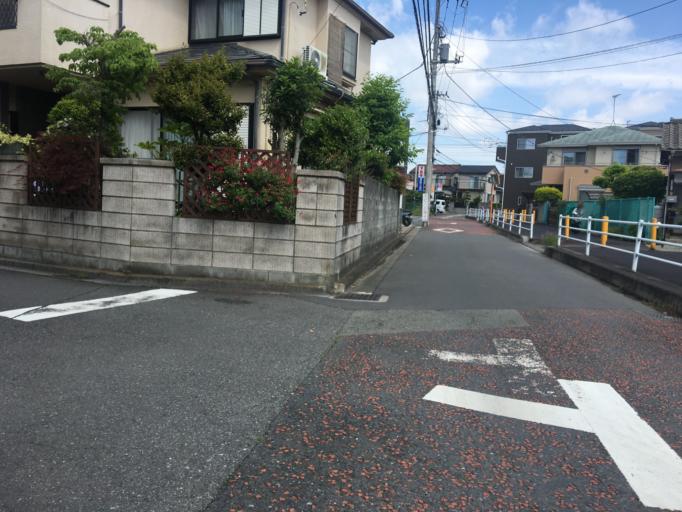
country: JP
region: Saitama
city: Yono
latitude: 35.8656
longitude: 139.6035
